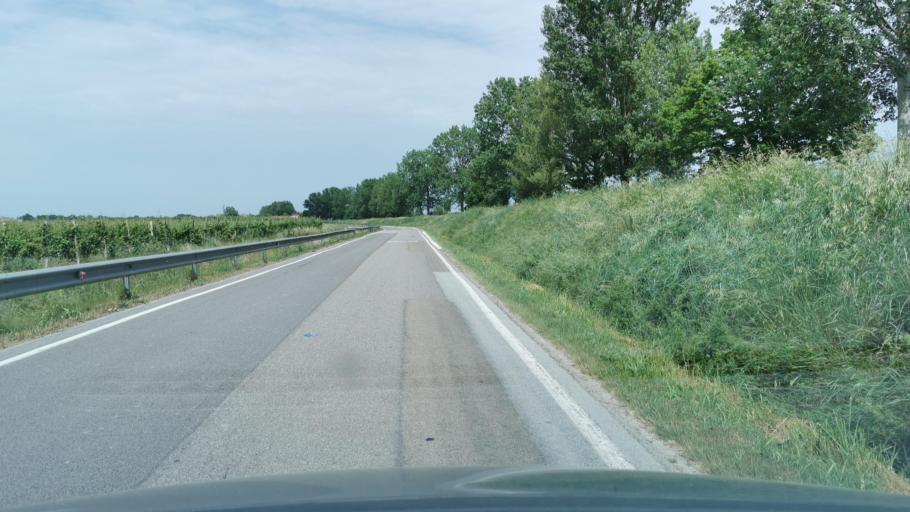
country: IT
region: Emilia-Romagna
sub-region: Provincia di Ravenna
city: Alfonsine
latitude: 44.4853
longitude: 12.0471
